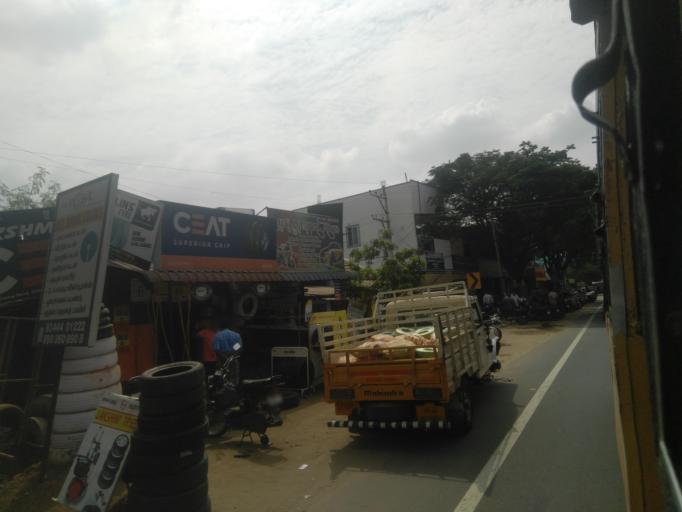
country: IN
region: Tamil Nadu
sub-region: Coimbatore
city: Irugur
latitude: 11.0084
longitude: 77.0762
